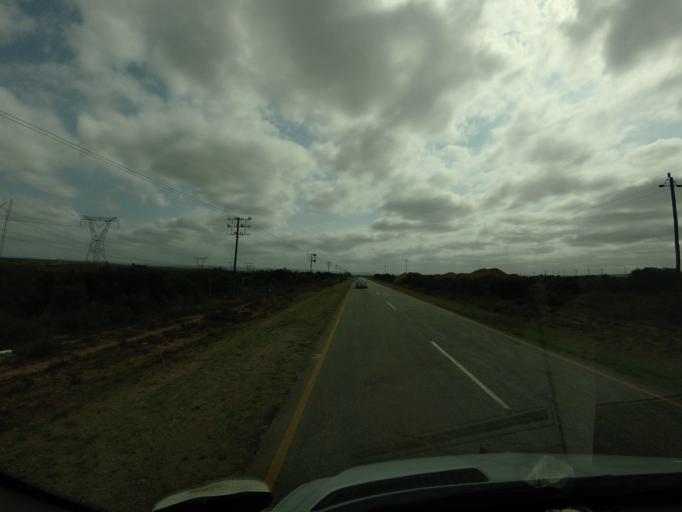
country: ZA
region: Eastern Cape
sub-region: Cacadu District Municipality
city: Kirkwood
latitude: -33.5000
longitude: 25.6974
